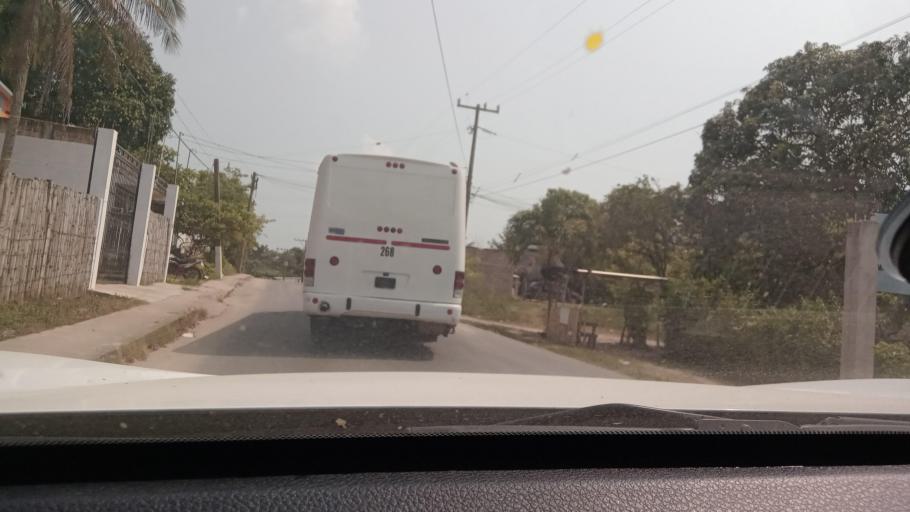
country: MX
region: Veracruz
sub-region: Minatitlan
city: Las Lomas
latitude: 17.9661
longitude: -94.5649
